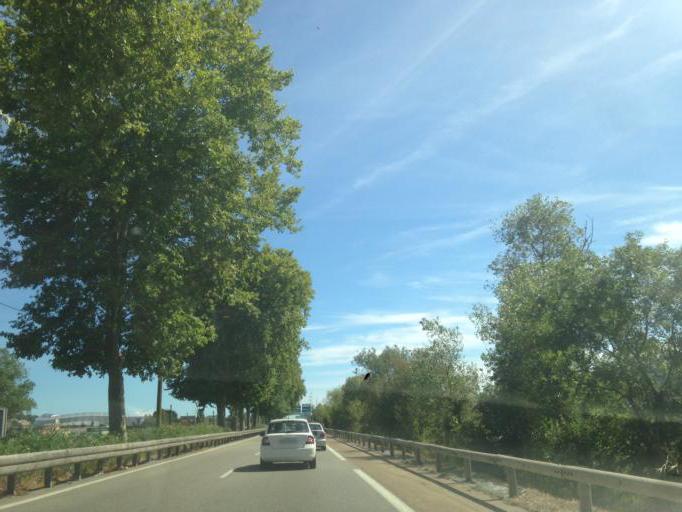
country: FR
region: Provence-Alpes-Cote d'Azur
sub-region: Departement des Alpes-Maritimes
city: La Gaude
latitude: 43.7155
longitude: 7.1869
